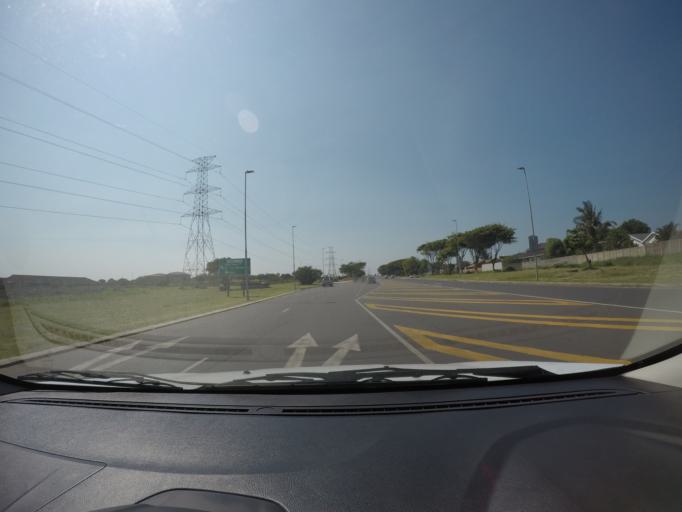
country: ZA
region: KwaZulu-Natal
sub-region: uThungulu District Municipality
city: Richards Bay
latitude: -28.7334
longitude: 32.0395
